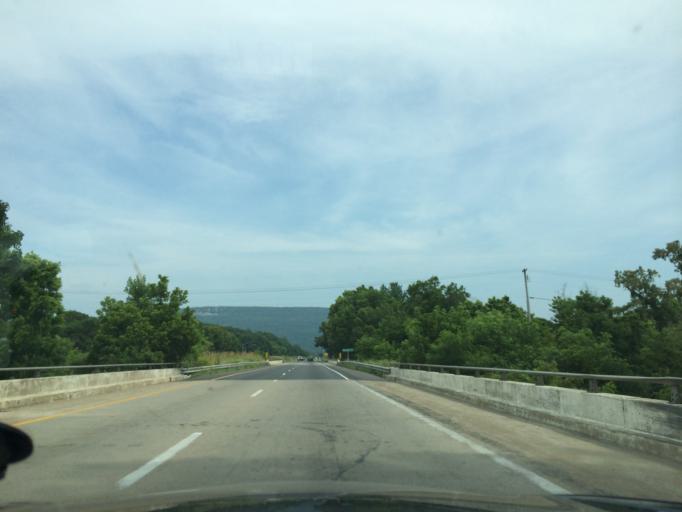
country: US
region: Maryland
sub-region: Washington County
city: Robinwood
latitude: 39.5865
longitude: -77.6415
